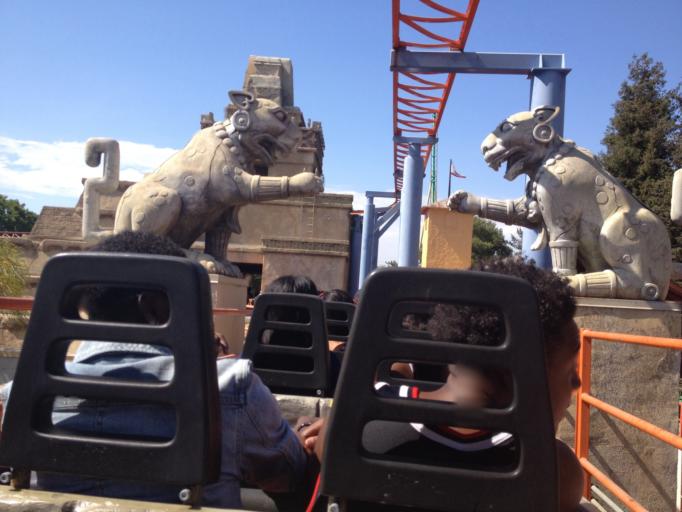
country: US
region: California
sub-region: Orange County
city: Buena Park
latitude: 33.8456
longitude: -117.9991
